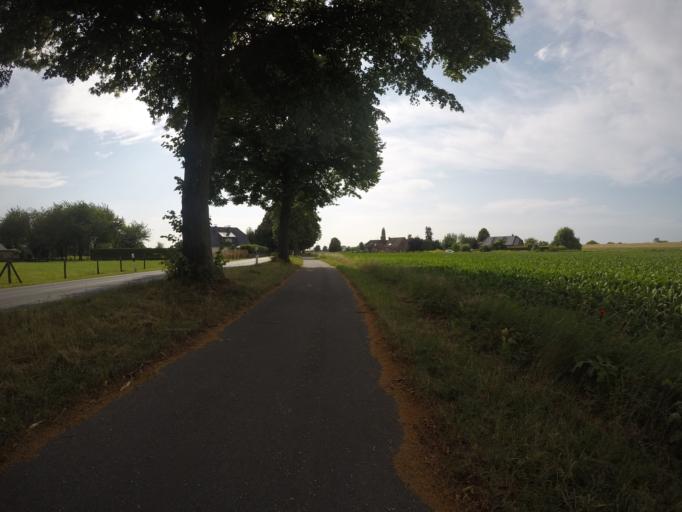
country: DE
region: North Rhine-Westphalia
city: Rees
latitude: 51.7484
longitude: 6.3690
